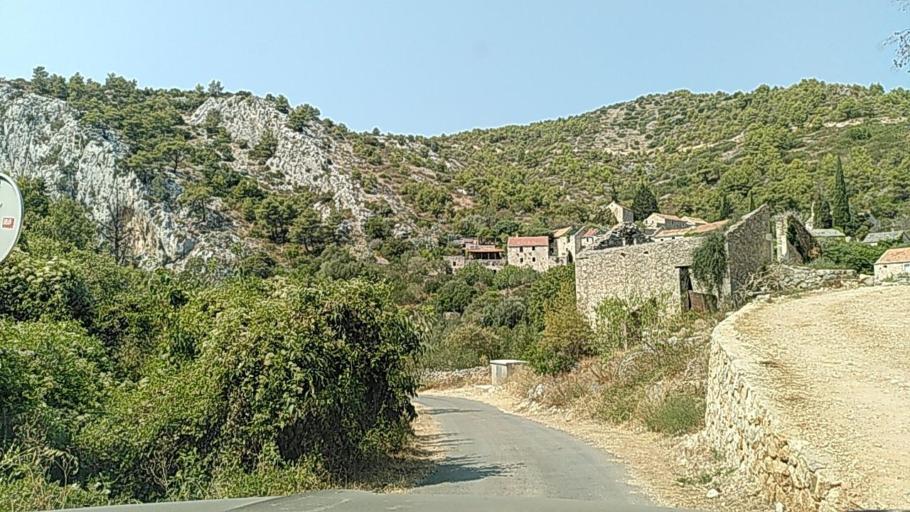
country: HR
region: Splitsko-Dalmatinska
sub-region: Grad Hvar
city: Hvar
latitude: 43.1675
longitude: 16.5036
